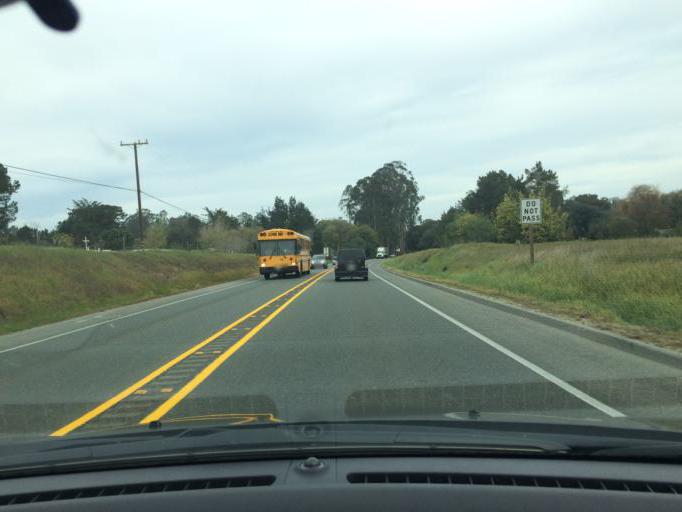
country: US
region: California
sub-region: Monterey County
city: Prunedale
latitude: 36.7868
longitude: -121.6836
